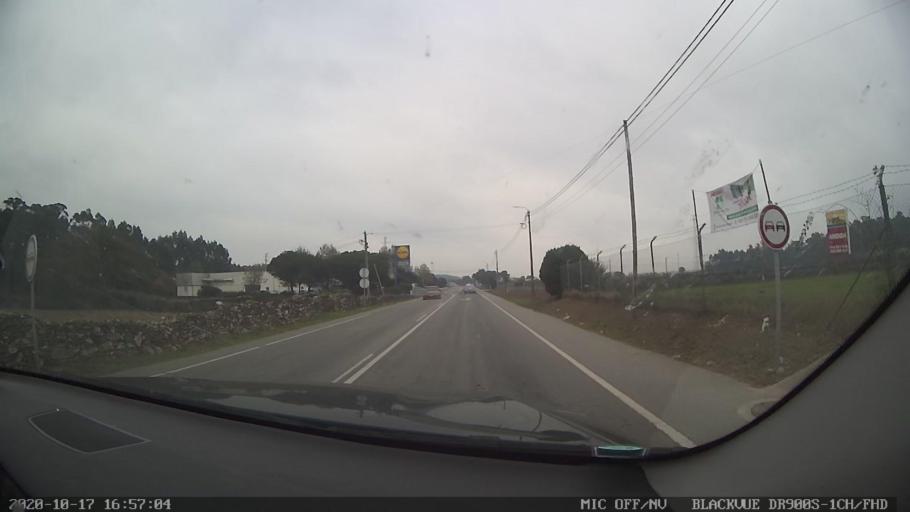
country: PT
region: Braga
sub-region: Esposende
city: Apulia
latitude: 41.5025
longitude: -8.7612
